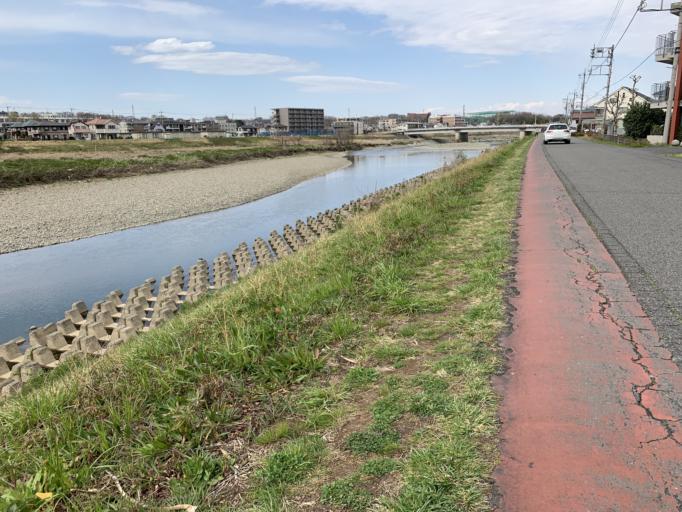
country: JP
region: Tokyo
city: Hino
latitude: 35.6571
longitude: 139.3916
